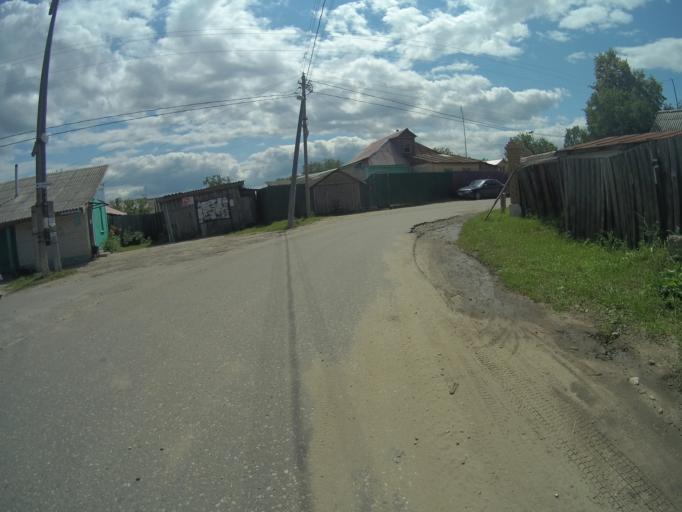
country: RU
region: Vladimir
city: Raduzhnyy
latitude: 56.0579
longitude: 40.3668
